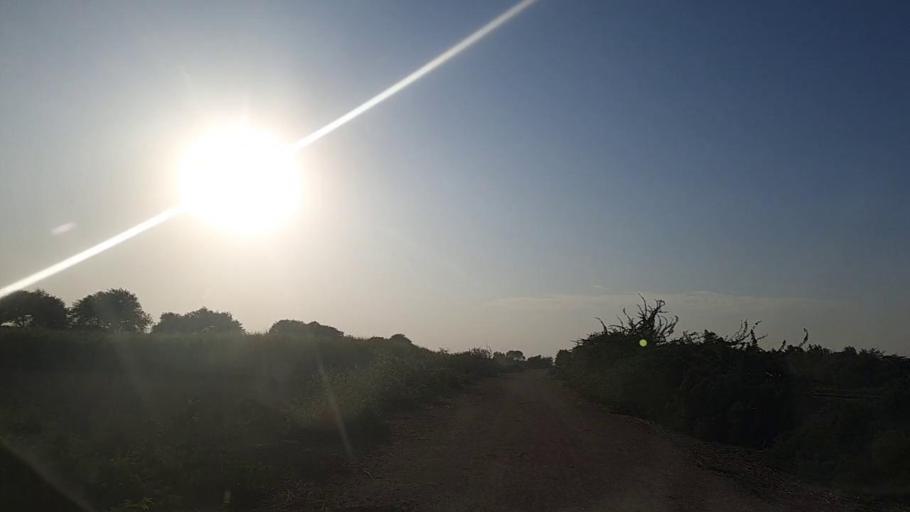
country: PK
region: Sindh
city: Jati
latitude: 24.4176
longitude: 68.1733
